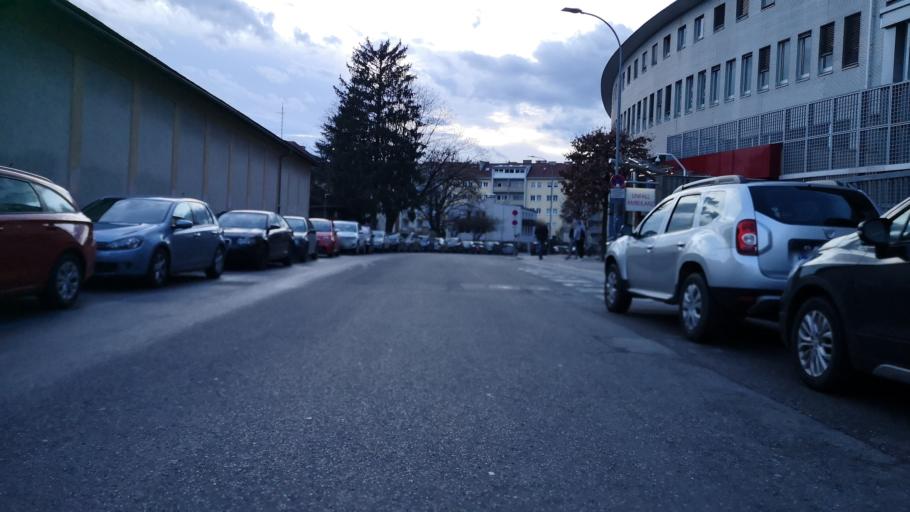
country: AT
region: Tyrol
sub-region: Innsbruck Stadt
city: Innsbruck
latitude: 47.2604
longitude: 11.3857
